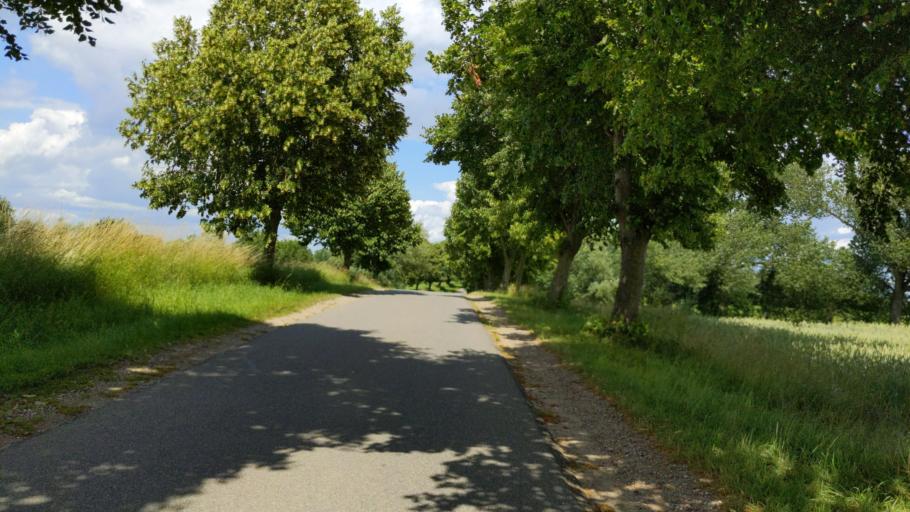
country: DE
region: Mecklenburg-Vorpommern
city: Kalkhorst
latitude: 53.9845
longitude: 11.0811
